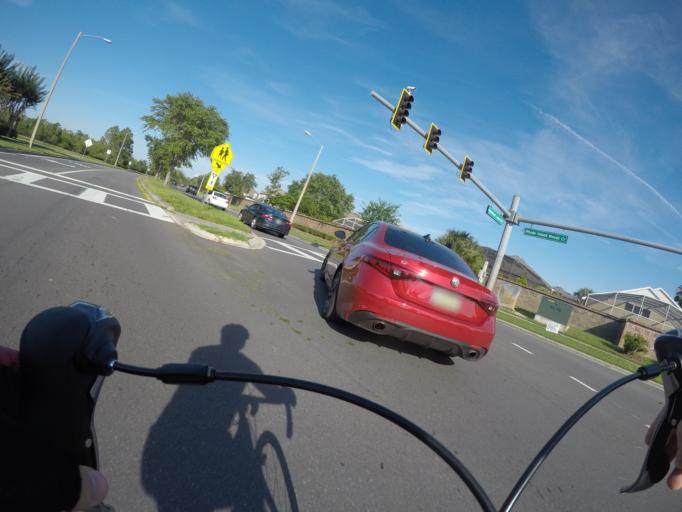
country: US
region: Florida
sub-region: Osceola County
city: Buenaventura Lakes
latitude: 28.3610
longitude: -81.3497
